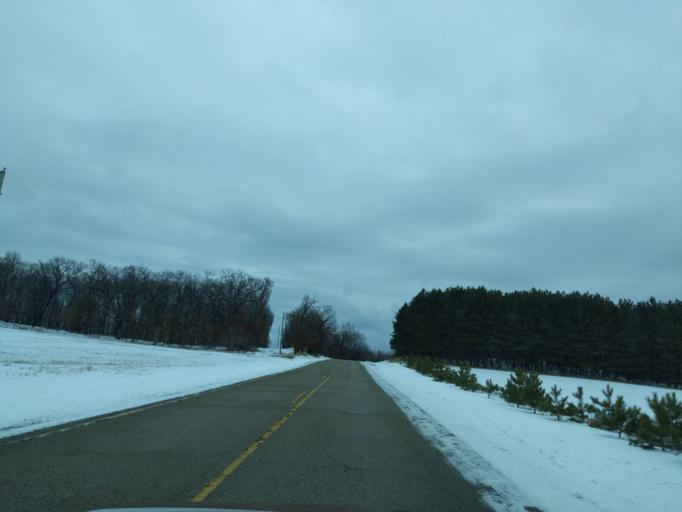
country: US
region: Wisconsin
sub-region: Marquette County
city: Montello
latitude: 43.9144
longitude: -89.3486
